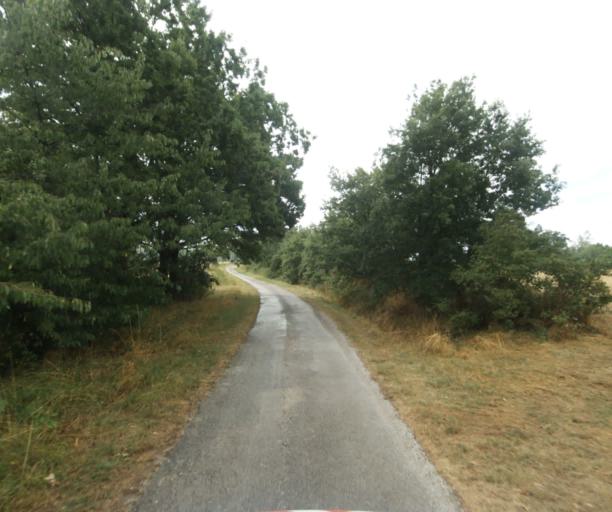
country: FR
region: Midi-Pyrenees
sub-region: Departement de la Haute-Garonne
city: Revel
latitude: 43.4215
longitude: 1.9772
